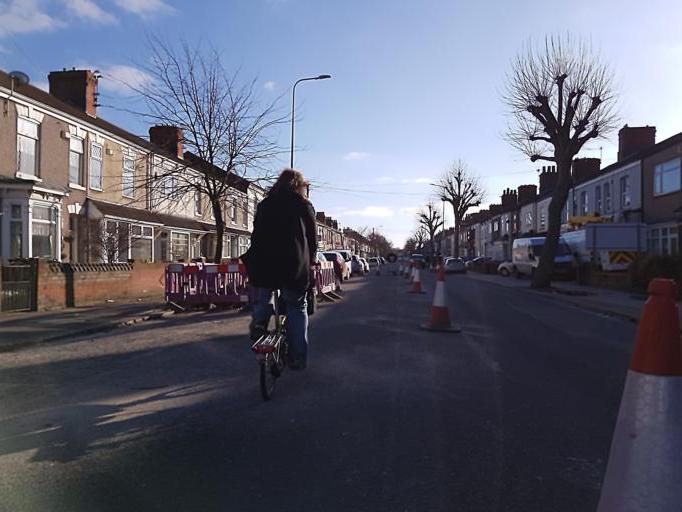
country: GB
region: England
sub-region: North East Lincolnshire
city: Grimsby
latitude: 53.5636
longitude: -0.0757
